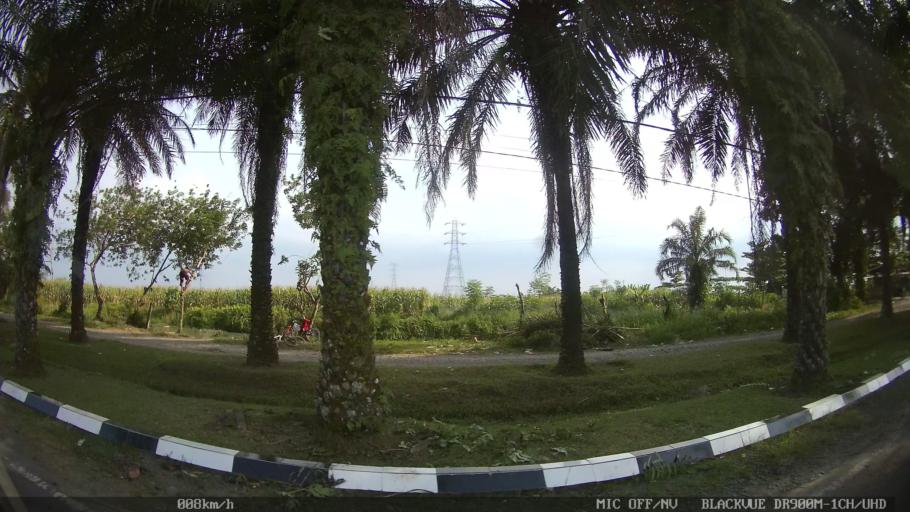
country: ID
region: North Sumatra
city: Binjai
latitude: 3.6030
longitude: 98.5112
